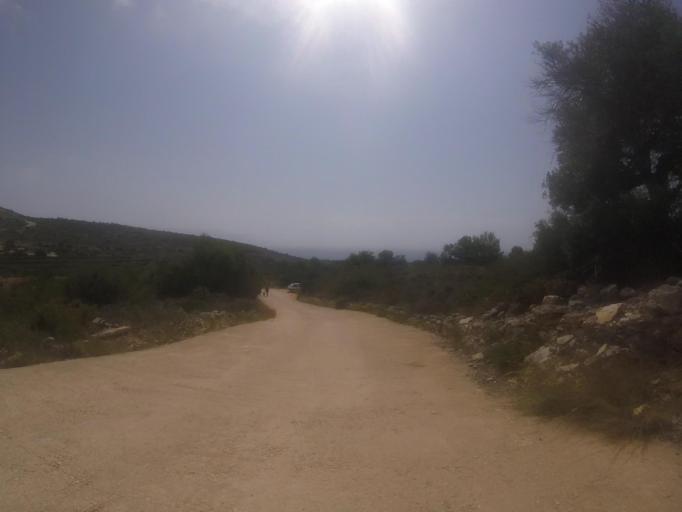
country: ES
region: Valencia
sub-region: Provincia de Castello
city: Peniscola
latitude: 40.3484
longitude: 0.3681
